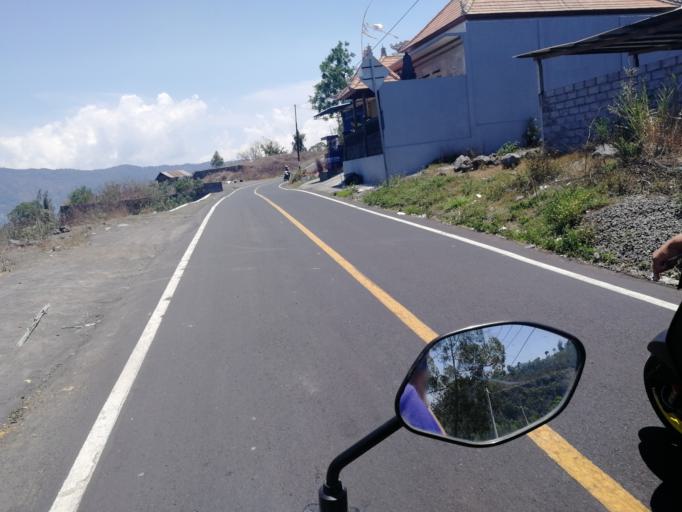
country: ID
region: Bali
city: Banjar Trunyan
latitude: -8.2313
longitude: 115.4063
